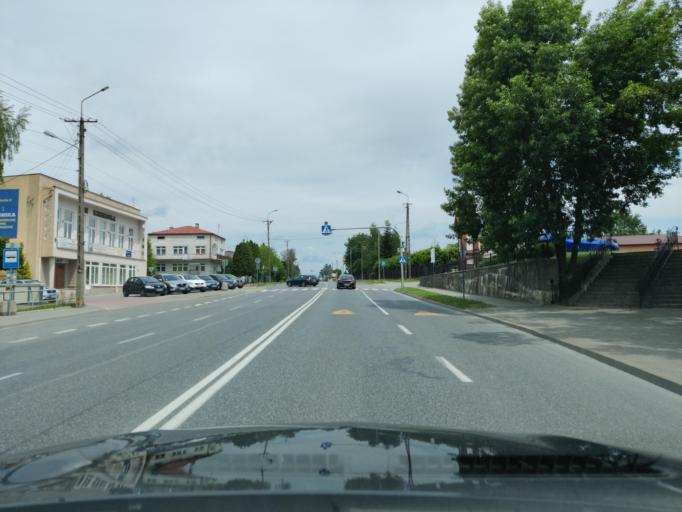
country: PL
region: Masovian Voivodeship
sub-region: Powiat wyszkowski
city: Wyszkow
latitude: 52.5942
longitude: 21.4595
